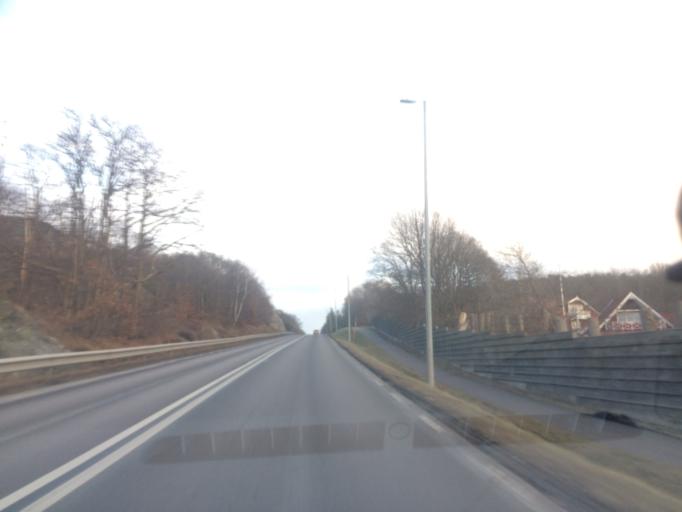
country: SE
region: Vaestra Goetaland
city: Hjuvik
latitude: 57.7116
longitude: 11.7269
